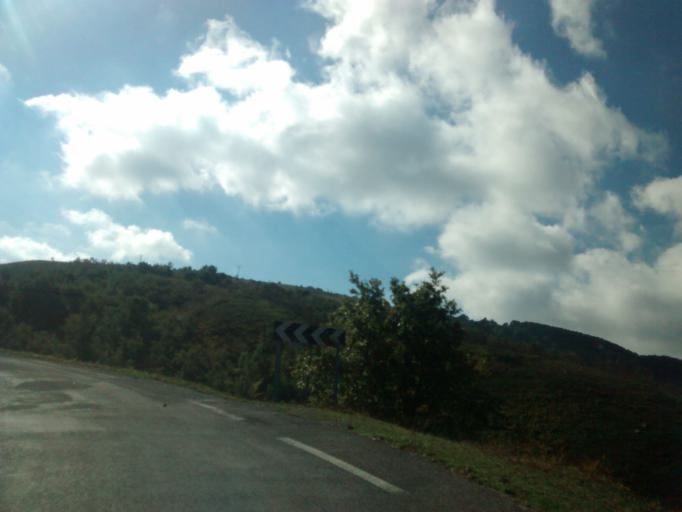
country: ES
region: Castille and Leon
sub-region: Provincia de Burgos
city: Arija
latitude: 42.9318
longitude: -4.0153
